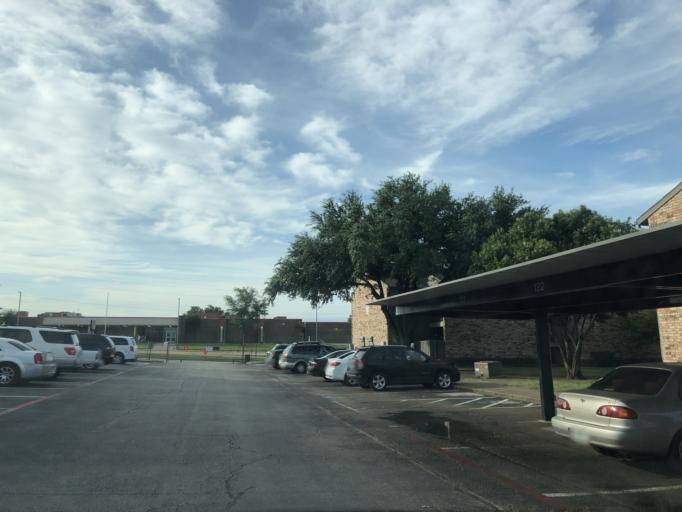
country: US
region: Texas
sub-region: Dallas County
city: Rowlett
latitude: 32.8509
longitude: -96.6072
